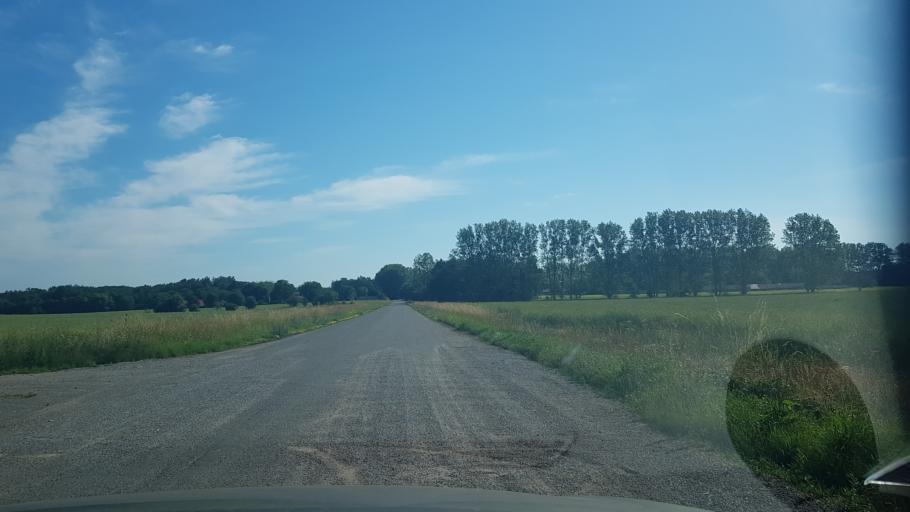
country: DK
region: Zealand
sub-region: Kalundborg Kommune
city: Svebolle
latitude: 55.6695
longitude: 11.2837
